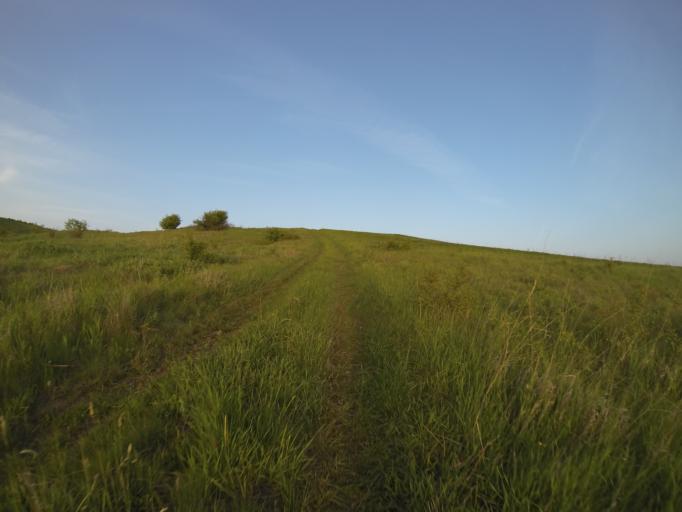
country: RO
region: Dolj
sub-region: Comuna Pielesti
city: Pielesti
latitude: 44.3585
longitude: 23.9708
